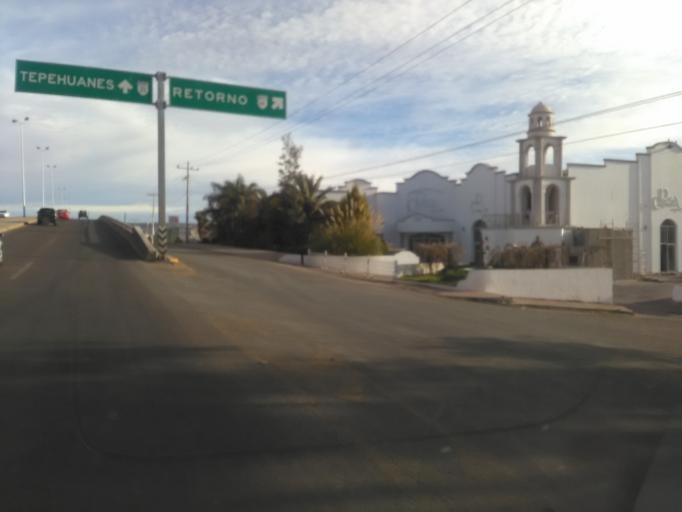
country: MX
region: Durango
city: Victoria de Durango
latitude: 24.0508
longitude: -104.6577
